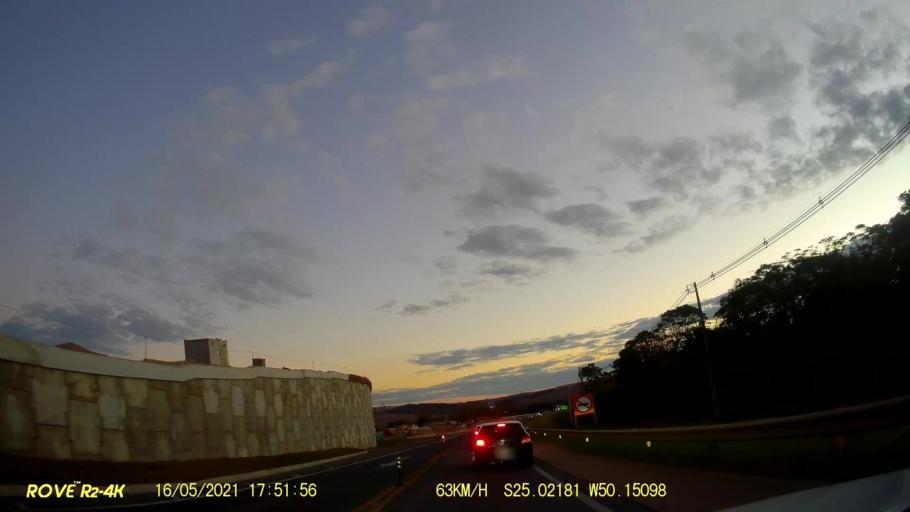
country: BR
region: Parana
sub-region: Ponta Grossa
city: Ponta Grossa
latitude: -25.0218
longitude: -50.1510
